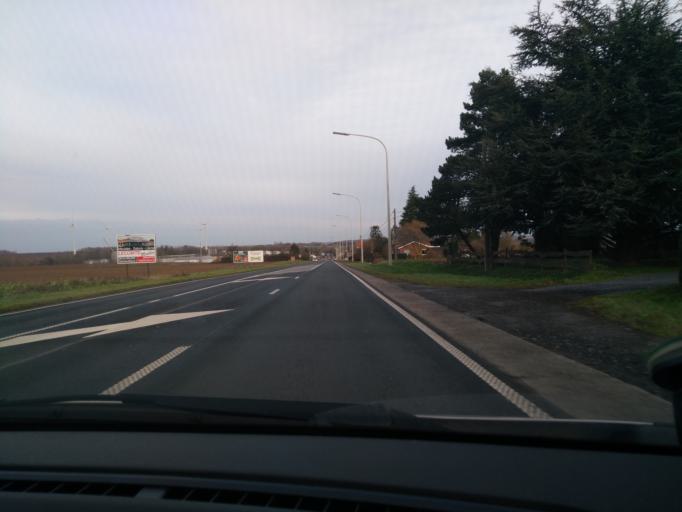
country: BE
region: Wallonia
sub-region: Province du Hainaut
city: Quevy-le-Petit
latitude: 50.3607
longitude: 3.9672
